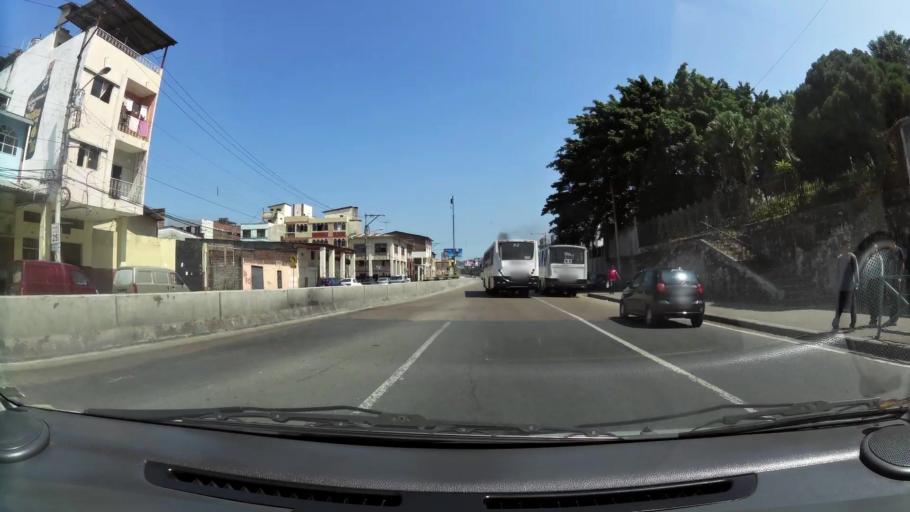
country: EC
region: Guayas
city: Eloy Alfaro
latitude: -2.1839
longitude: -79.8839
